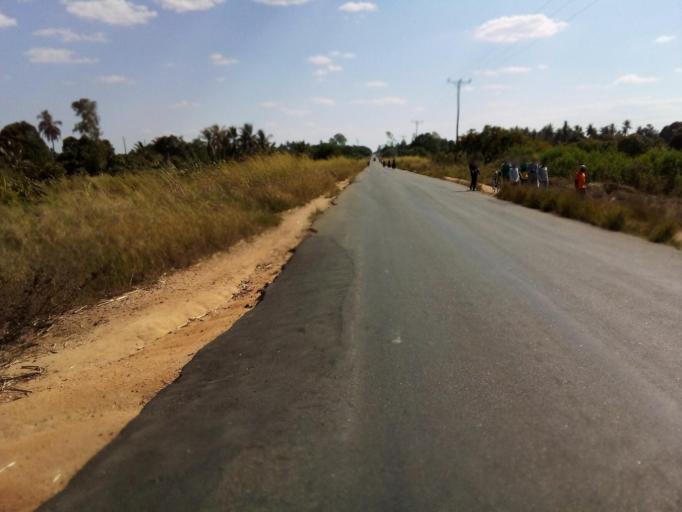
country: MZ
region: Zambezia
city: Quelimane
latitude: -17.5778
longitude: 36.6785
